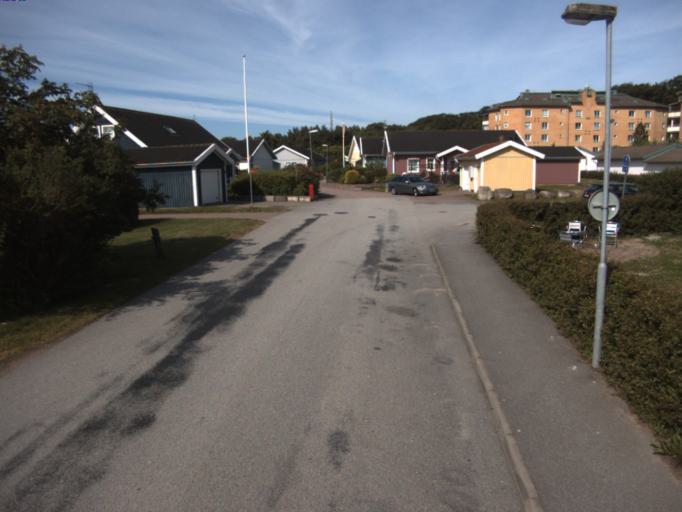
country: SE
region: Skane
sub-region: Helsingborg
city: Helsingborg
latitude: 56.0450
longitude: 12.7524
